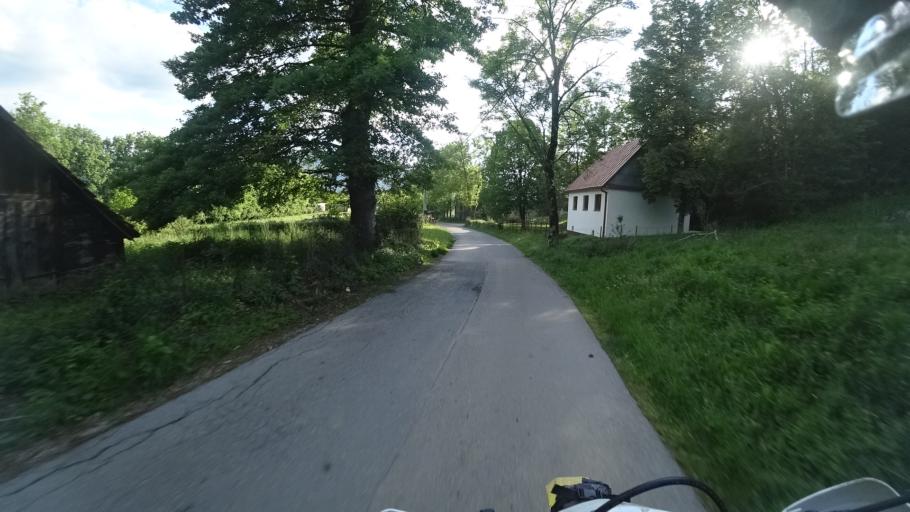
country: HR
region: Licko-Senjska
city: Gospic
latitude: 44.5174
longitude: 15.3341
